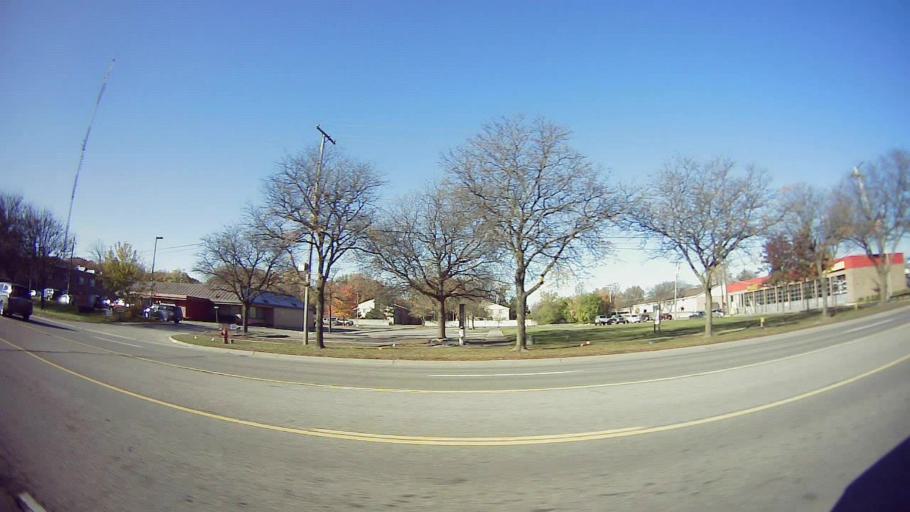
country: US
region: Michigan
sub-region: Oakland County
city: Lathrup Village
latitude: 42.4873
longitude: -83.2022
